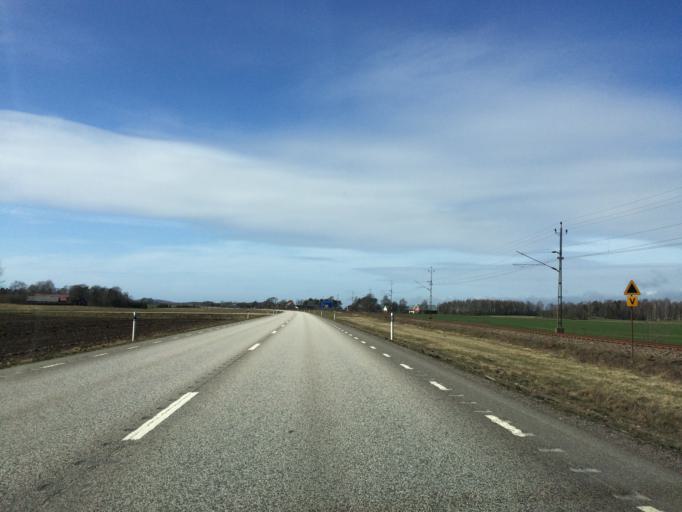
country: SE
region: Halland
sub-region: Laholms Kommun
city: Veinge
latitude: 56.5388
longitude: 13.1560
